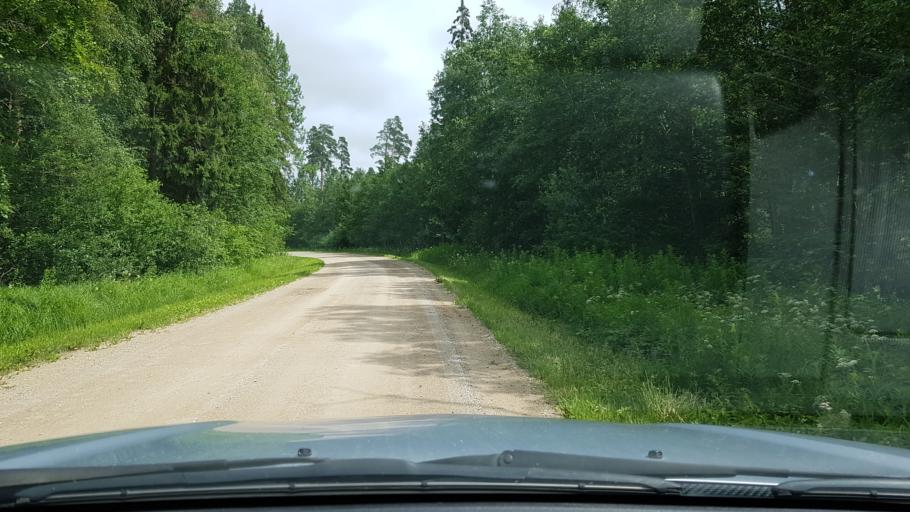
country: EE
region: Ida-Virumaa
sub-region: Narva-Joesuu linn
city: Narva-Joesuu
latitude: 59.3630
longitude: 28.0609
